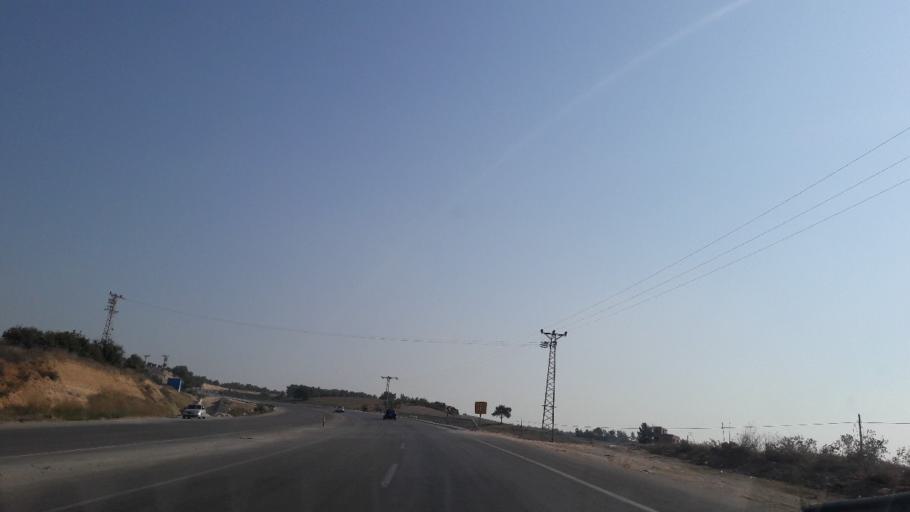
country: TR
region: Adana
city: Yuregir
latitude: 37.0750
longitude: 35.4681
